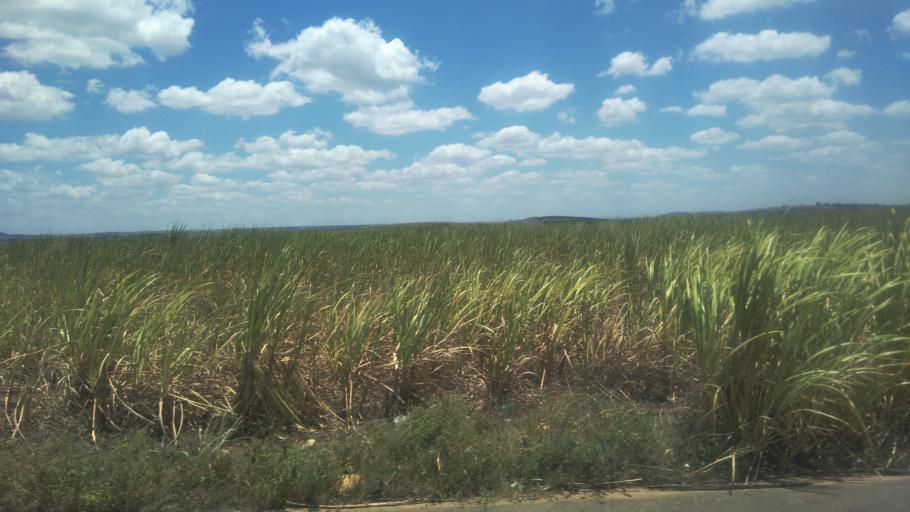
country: BR
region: Pernambuco
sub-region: Nazare Da Mata
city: Nazare da Mata
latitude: -7.7333
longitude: -35.2556
